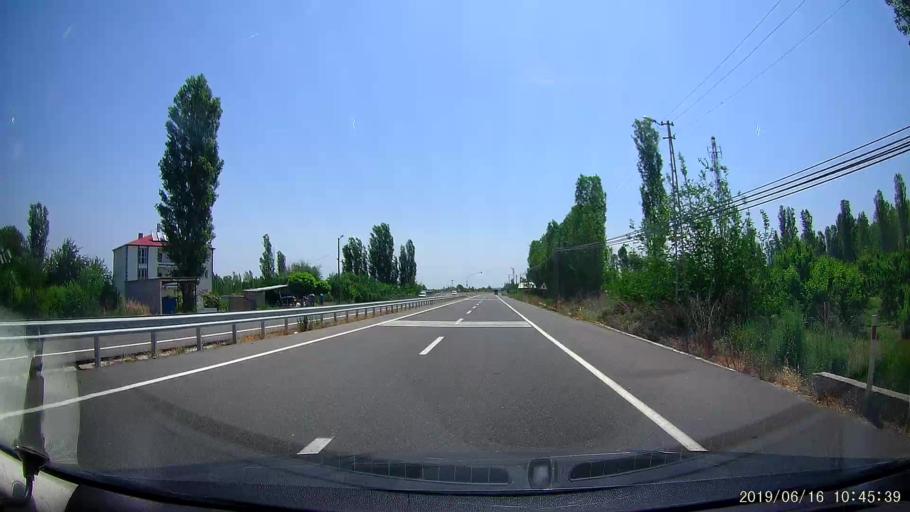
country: AM
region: Armavir
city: Shenavan
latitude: 40.0269
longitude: 43.8717
